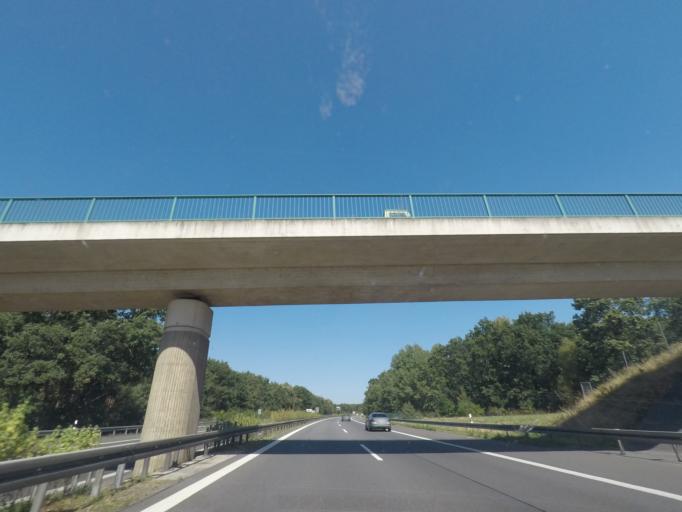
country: DE
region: Brandenburg
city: Bronkow
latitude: 51.6691
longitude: 13.9043
